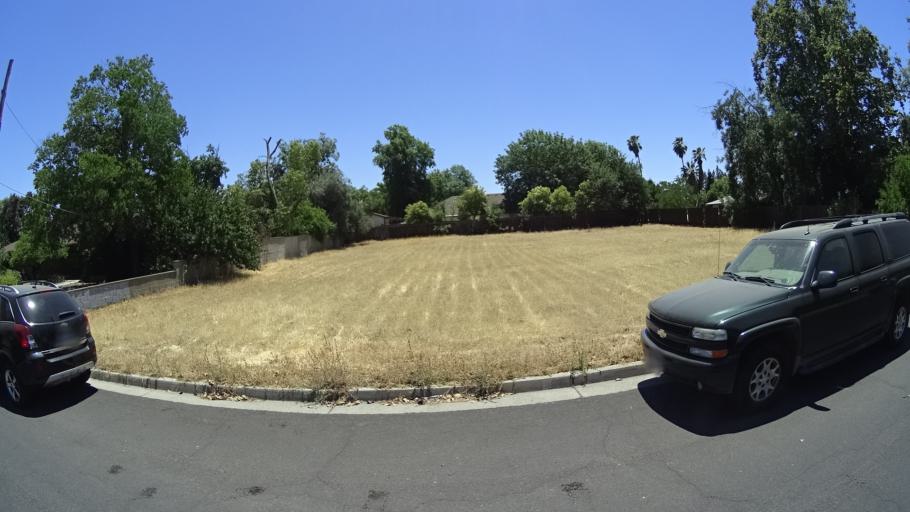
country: US
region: California
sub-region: Fresno County
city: Tarpey Village
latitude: 36.8050
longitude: -119.7526
